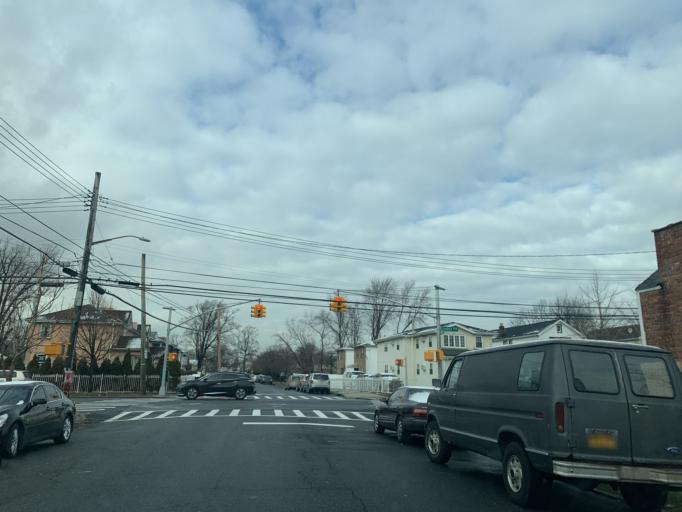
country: US
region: New York
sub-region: Queens County
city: Jamaica
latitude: 40.6907
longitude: -73.7806
